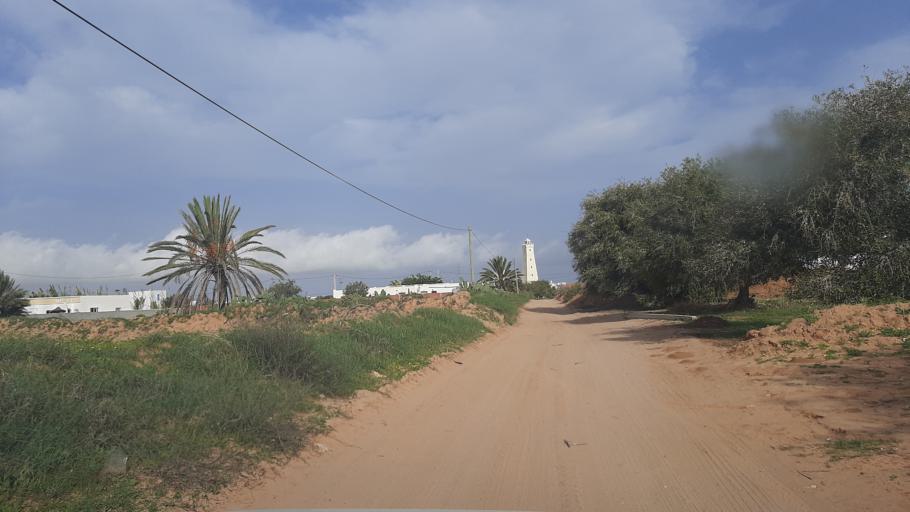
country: TN
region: Madanin
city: Midoun
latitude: 33.7963
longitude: 11.0295
